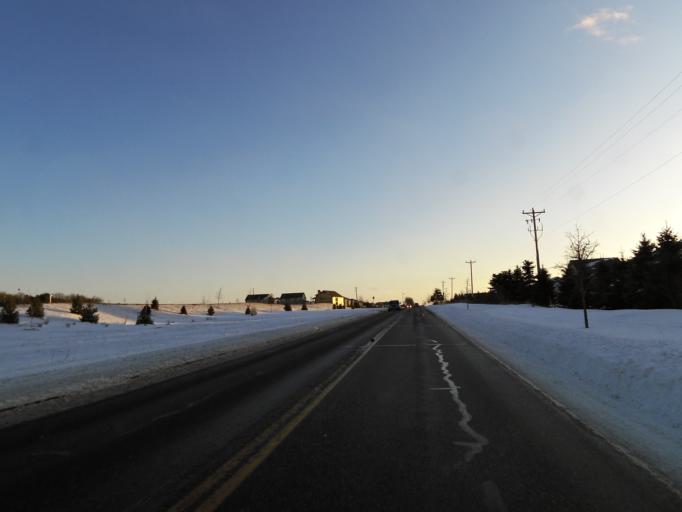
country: US
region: Minnesota
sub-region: Washington County
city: Lake Elmo
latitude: 44.9368
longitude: -92.8833
